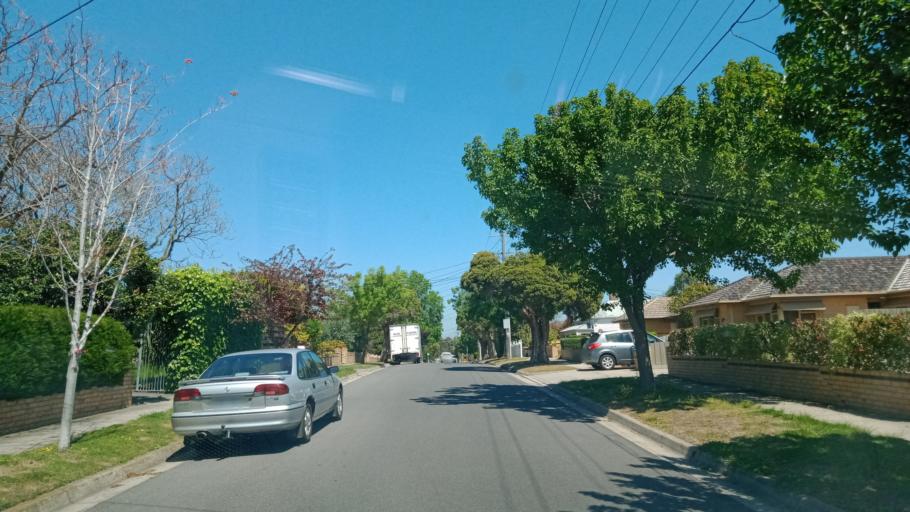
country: AU
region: Victoria
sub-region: Monash
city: Oakleigh South
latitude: -37.9244
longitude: 145.0751
